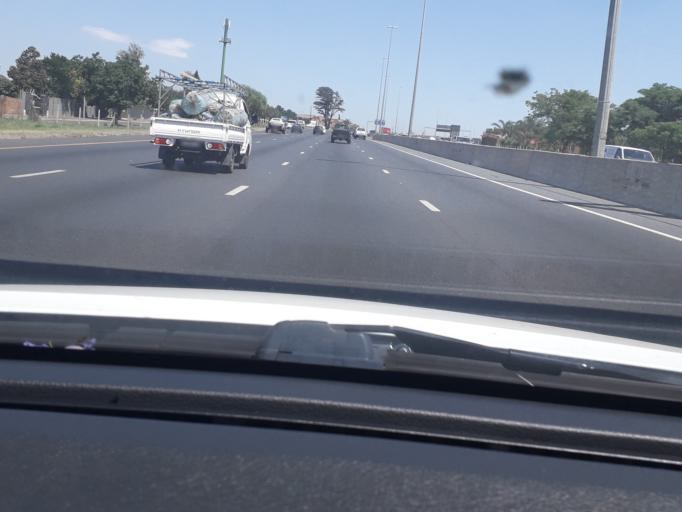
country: ZA
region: Gauteng
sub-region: Ekurhuleni Metropolitan Municipality
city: Germiston
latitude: -26.1794
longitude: 28.2053
